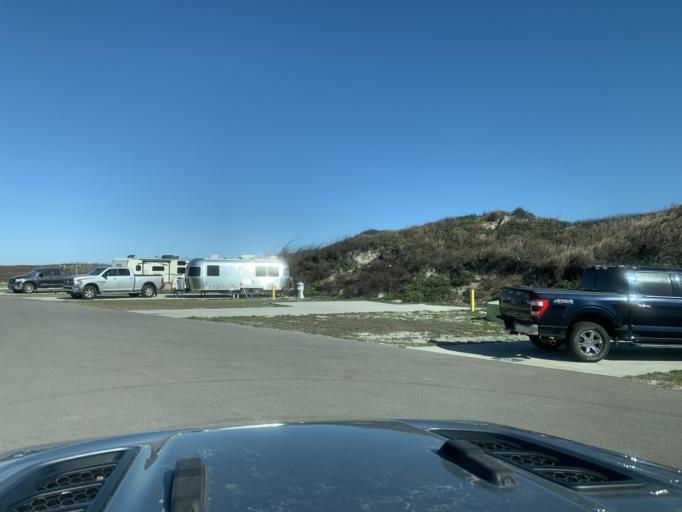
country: US
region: Texas
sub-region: Nueces County
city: Port Aransas
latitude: 27.8325
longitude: -97.0499
